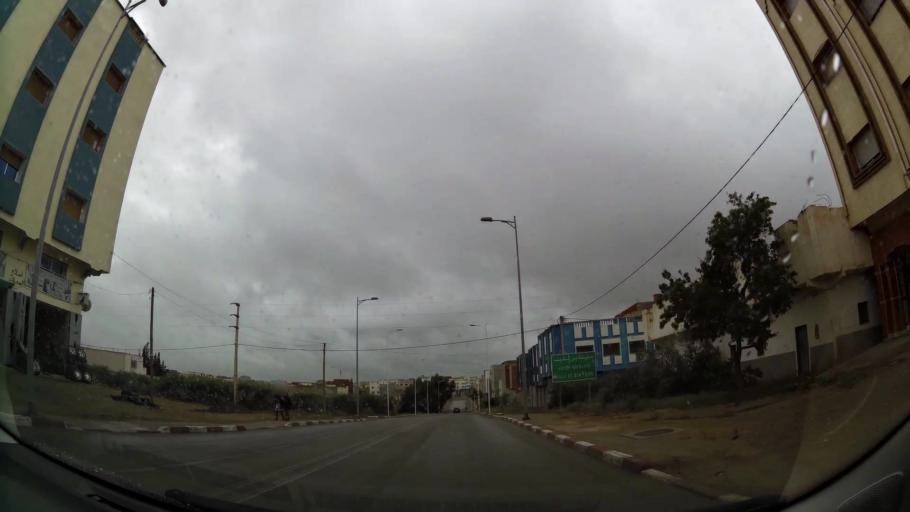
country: MA
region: Oriental
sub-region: Nador
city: Midar
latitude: 35.0494
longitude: -3.4494
